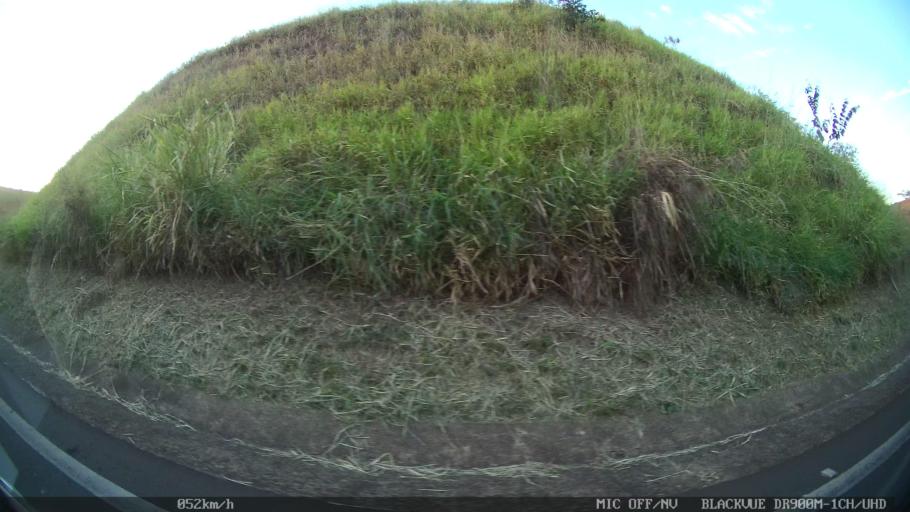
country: BR
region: Sao Paulo
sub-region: Pindorama
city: Pindorama
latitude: -21.2085
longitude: -48.9326
